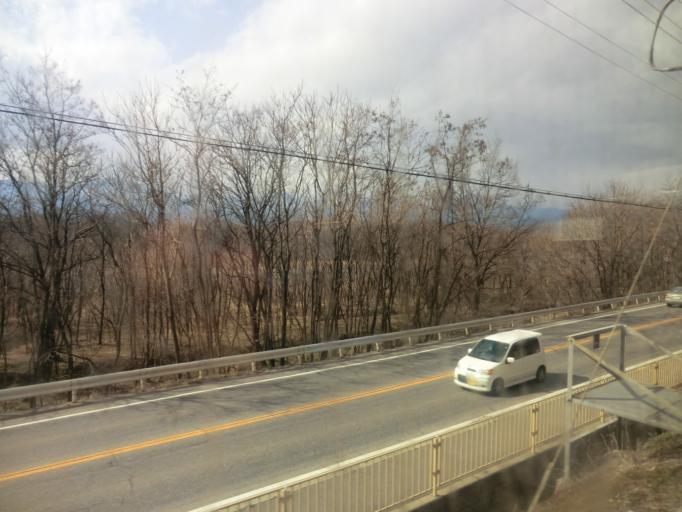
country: JP
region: Nagano
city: Toyoshina
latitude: 36.2883
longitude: 137.9449
